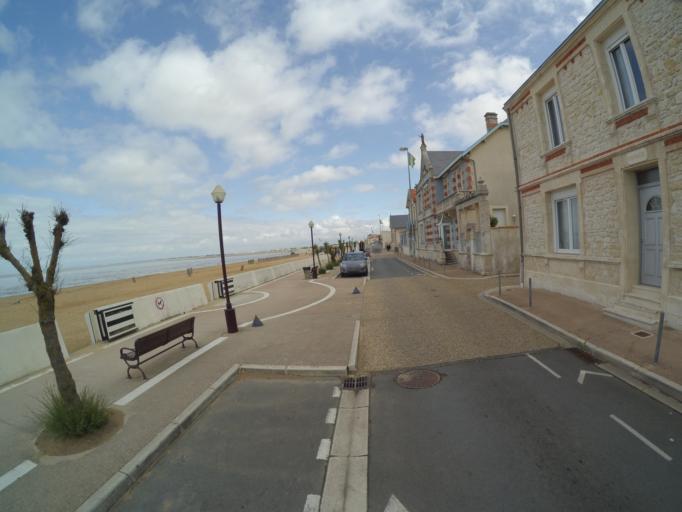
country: FR
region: Poitou-Charentes
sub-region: Departement de la Charente-Maritime
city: Chatelaillon-Plage
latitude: 46.0723
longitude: -1.0931
